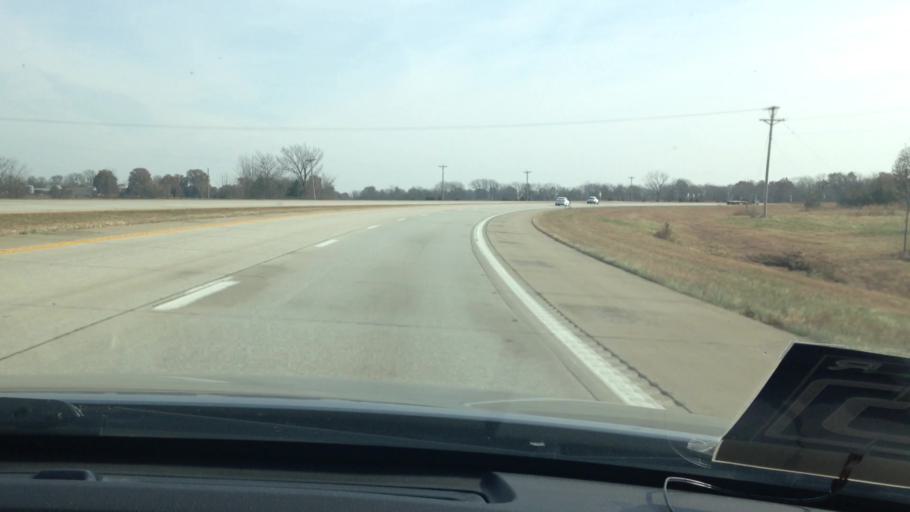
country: US
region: Missouri
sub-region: Henry County
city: Clinton
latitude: 38.4636
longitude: -93.9735
